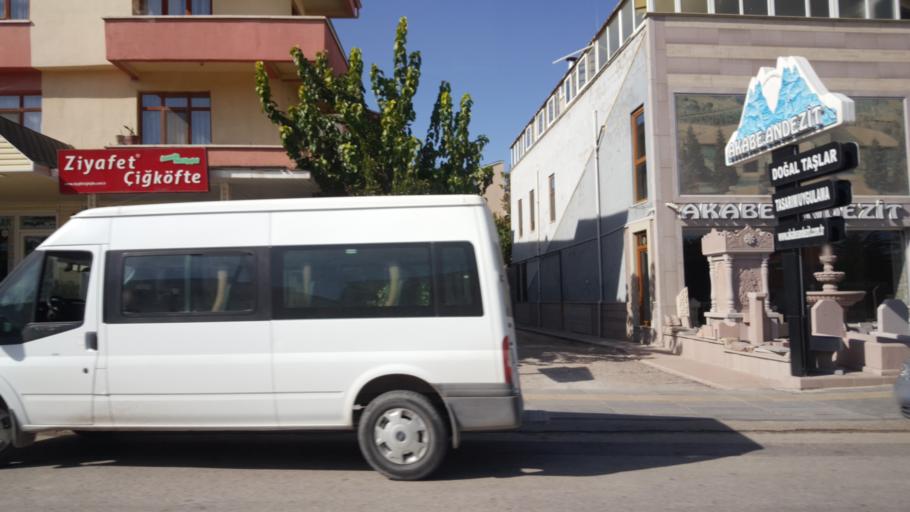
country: TR
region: Ankara
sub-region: Goelbasi
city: Golbasi
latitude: 39.7975
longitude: 32.7986
